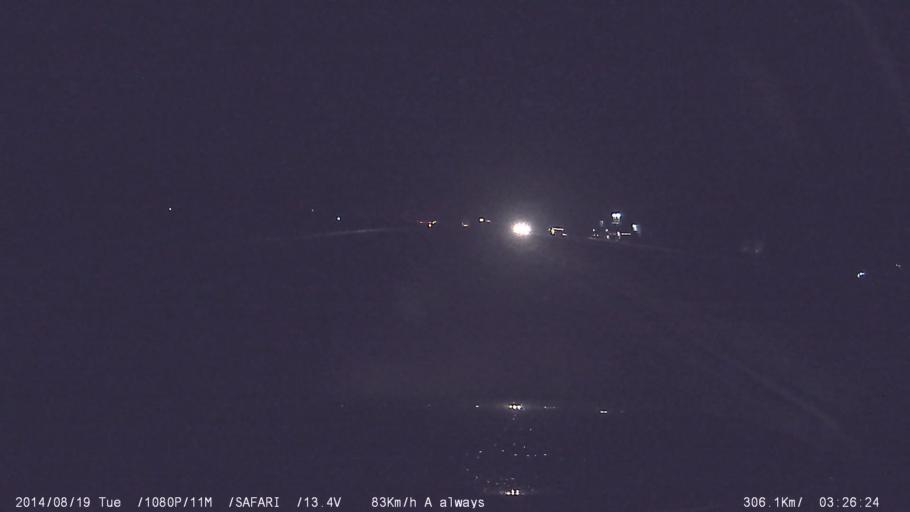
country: IN
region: Tamil Nadu
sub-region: Tiruppur
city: Avinashi
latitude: 11.1755
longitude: 77.2615
